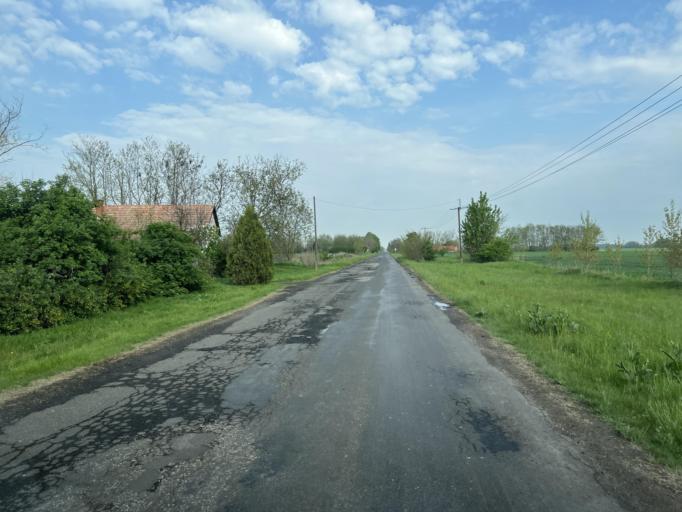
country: HU
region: Pest
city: Abony
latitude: 47.1584
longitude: 20.0492
